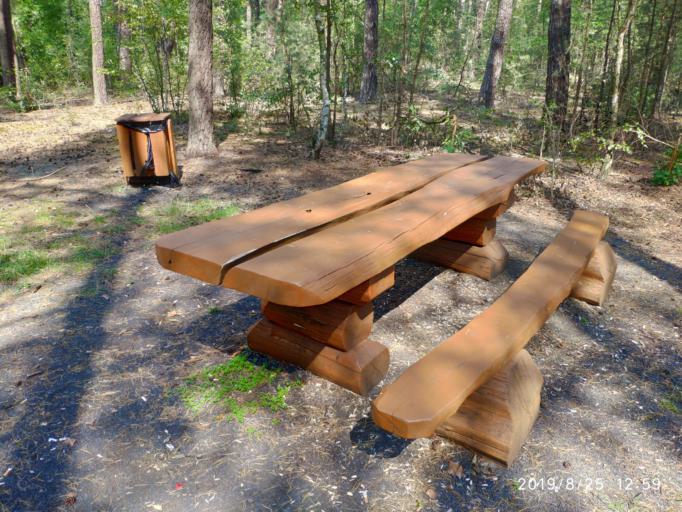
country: PL
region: Lubusz
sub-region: Powiat krosnienski
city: Dabie
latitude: 51.9929
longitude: 15.1638
